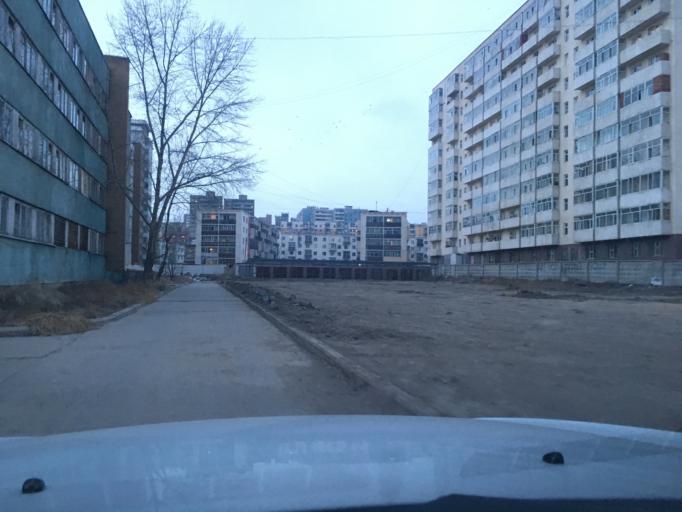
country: MN
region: Ulaanbaatar
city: Ulaanbaatar
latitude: 47.9151
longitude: 106.8612
